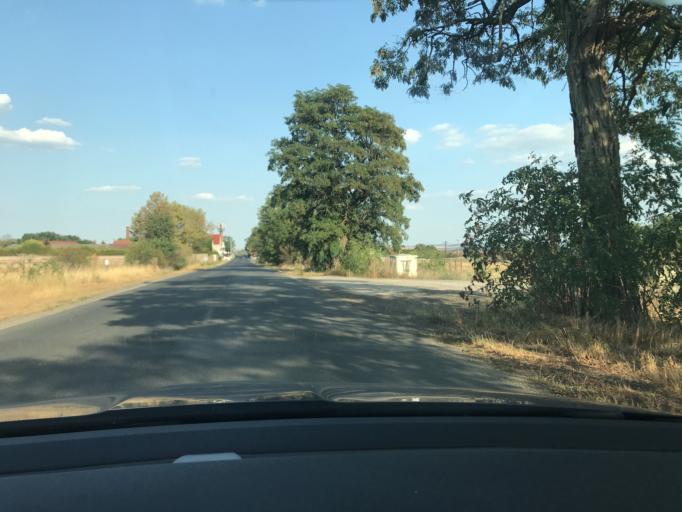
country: CZ
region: Ustecky
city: Postoloprty
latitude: 50.3623
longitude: 13.6855
